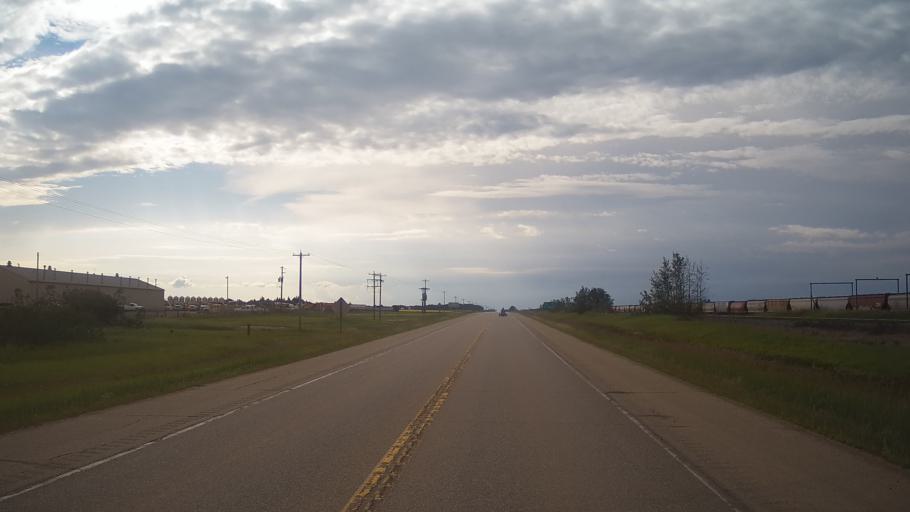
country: CA
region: Alberta
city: Viking
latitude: 53.0986
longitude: -111.7966
